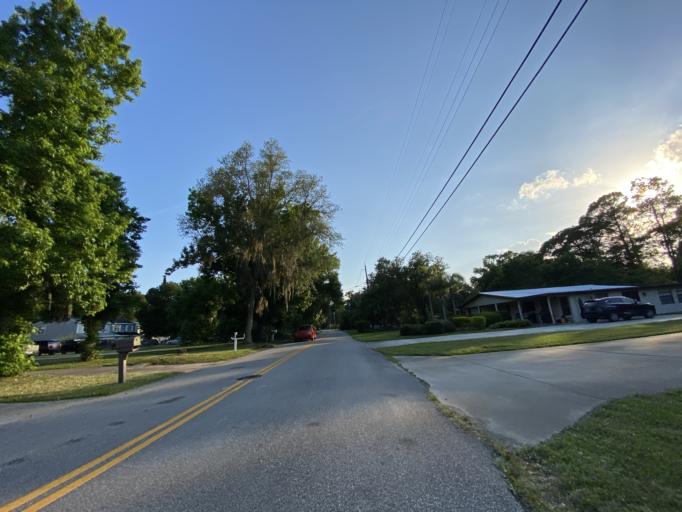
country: US
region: Florida
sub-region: Volusia County
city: Port Orange
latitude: 29.1450
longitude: -81.0019
